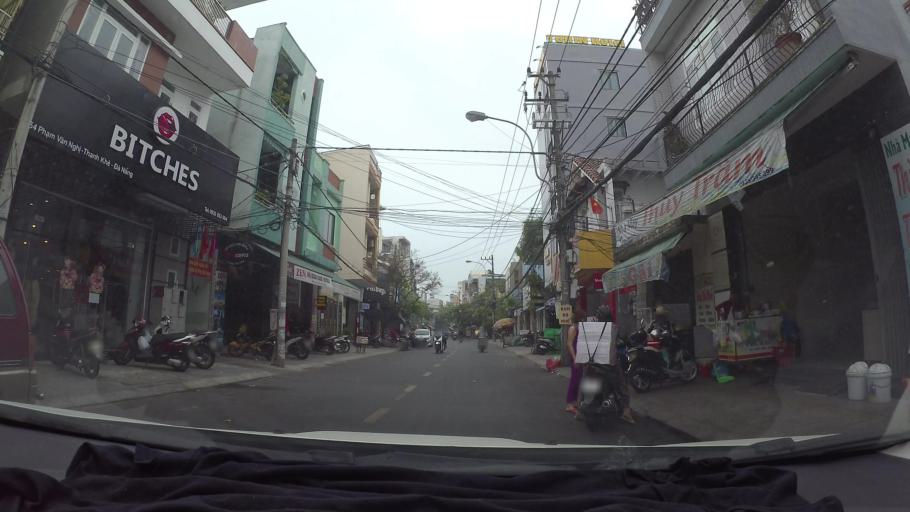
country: VN
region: Da Nang
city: Da Nang
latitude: 16.0572
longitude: 108.2100
